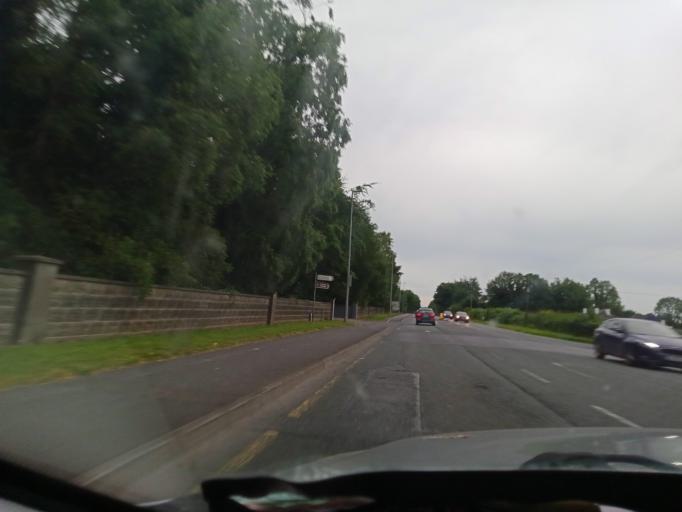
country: IE
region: Leinster
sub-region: Laois
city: Portlaoise
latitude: 53.0165
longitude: -7.3017
